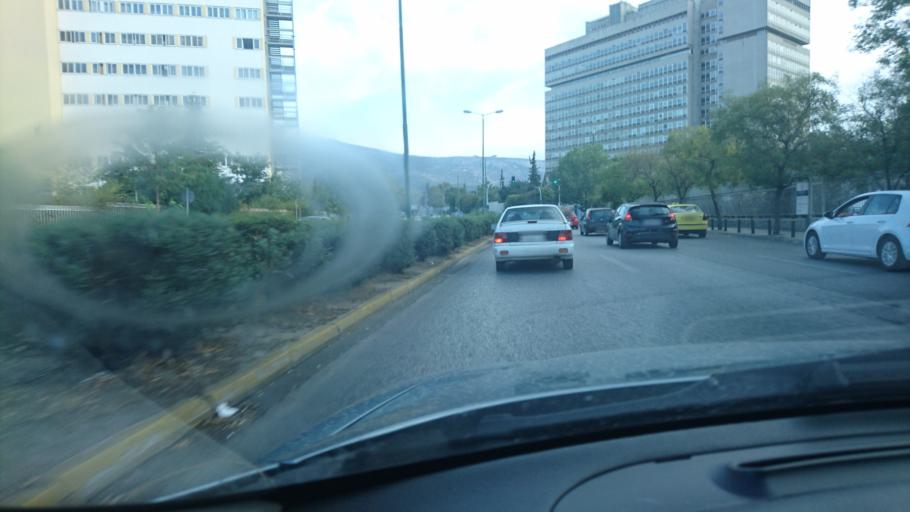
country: GR
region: Attica
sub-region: Nomarchia Athinas
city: Neo Psychiko
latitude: 37.9916
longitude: 23.7768
